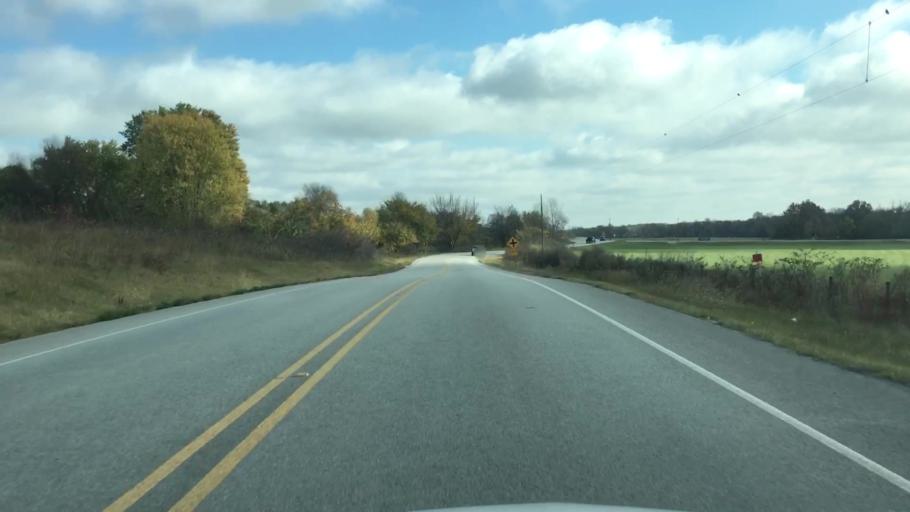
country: US
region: Arkansas
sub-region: Benton County
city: Centerton
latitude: 36.3016
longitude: -94.3110
